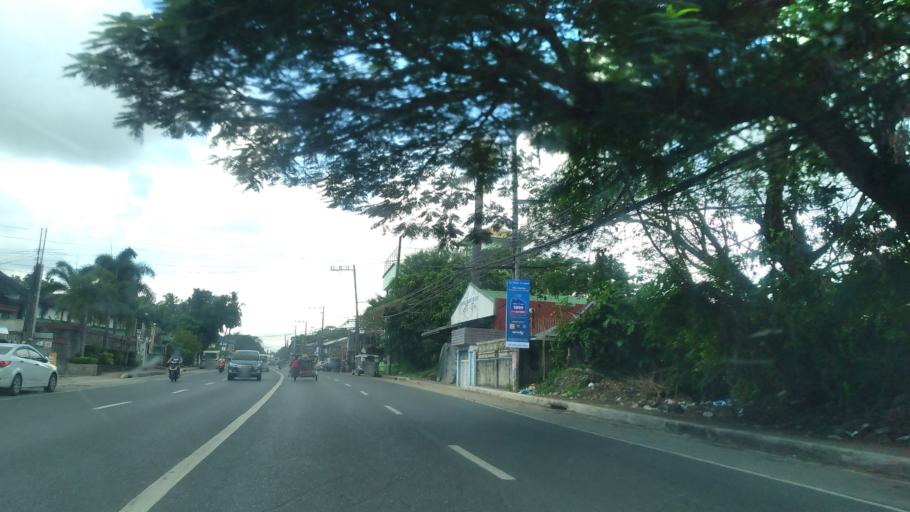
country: PH
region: Calabarzon
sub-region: Province of Quezon
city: Isabang
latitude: 13.9464
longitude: 121.5891
